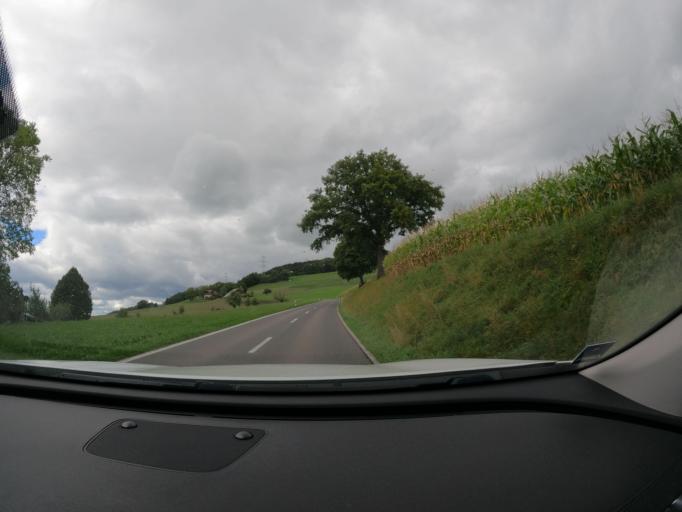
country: CH
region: Lucerne
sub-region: Sursee District
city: Bueron
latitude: 47.2201
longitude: 8.0986
